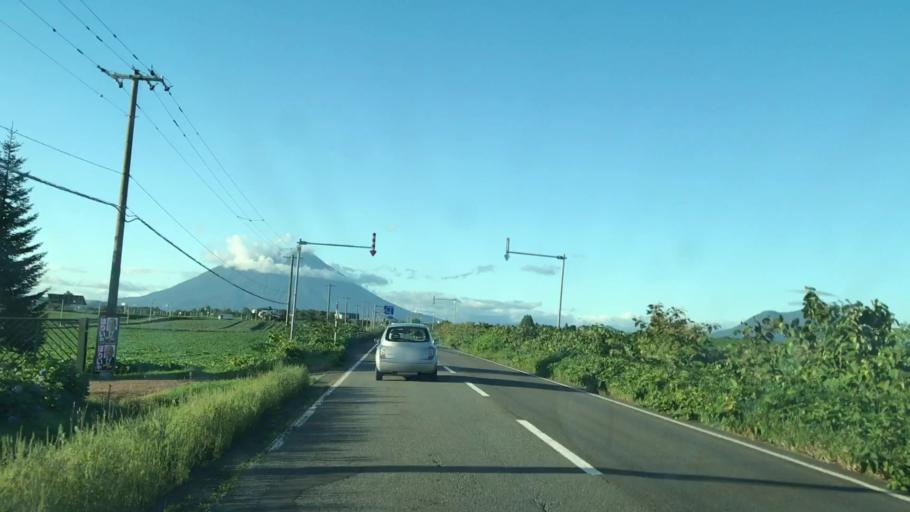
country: JP
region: Hokkaido
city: Niseko Town
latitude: 42.6572
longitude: 140.8113
